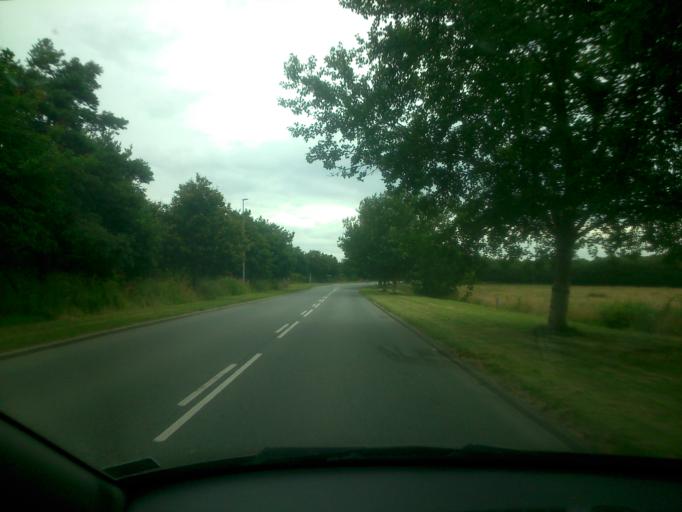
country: DK
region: South Denmark
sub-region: Esbjerg Kommune
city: Esbjerg
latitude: 55.5177
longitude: 8.4250
